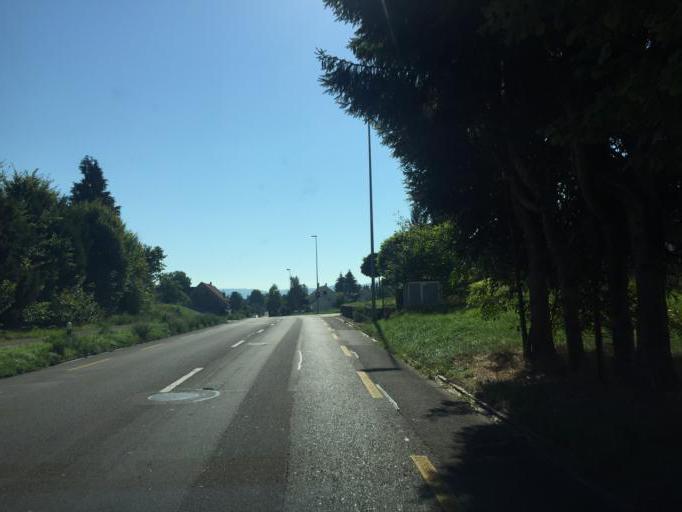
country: CH
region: Thurgau
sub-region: Frauenfeld District
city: Wagenhausen
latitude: 47.6615
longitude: 8.8419
